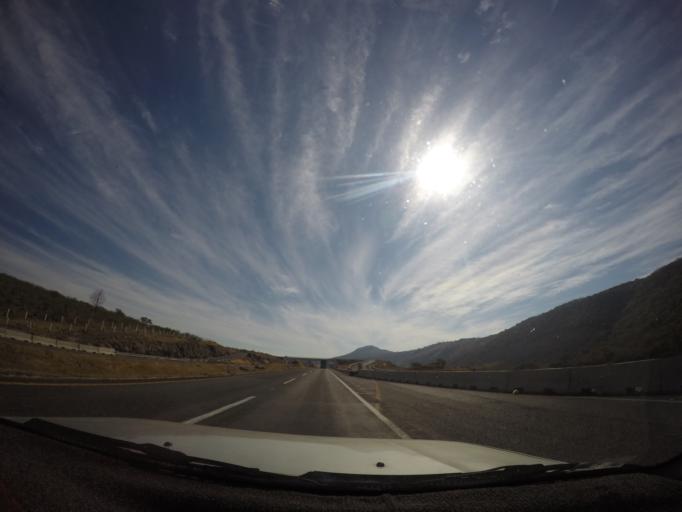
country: MX
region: Jalisco
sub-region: Zapotlan del Rey
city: Zapotlan del Rey
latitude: 20.5020
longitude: -102.9535
